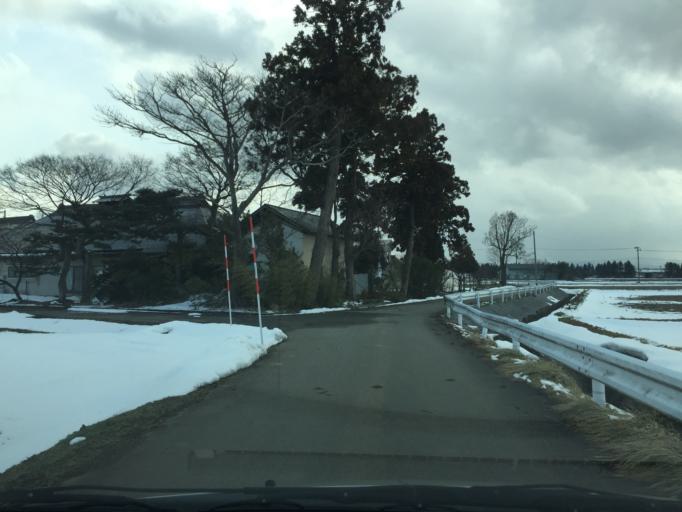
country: JP
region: Fukushima
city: Kitakata
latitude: 37.5372
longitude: 139.9077
